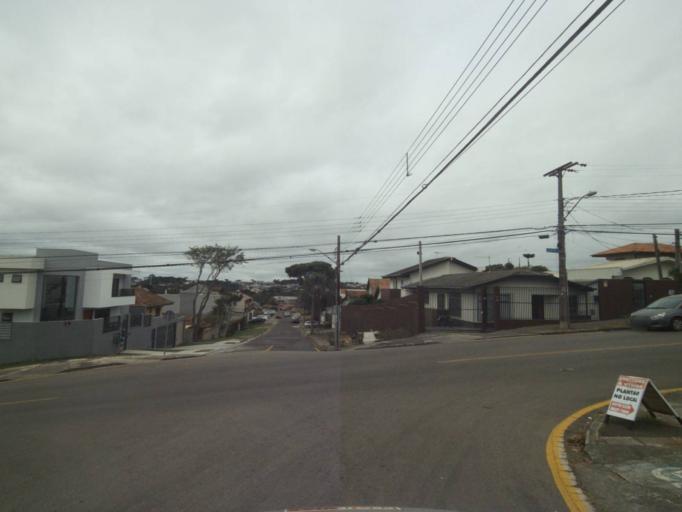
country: BR
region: Parana
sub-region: Sao Jose Dos Pinhais
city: Sao Jose dos Pinhais
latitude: -25.4852
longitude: -49.2292
